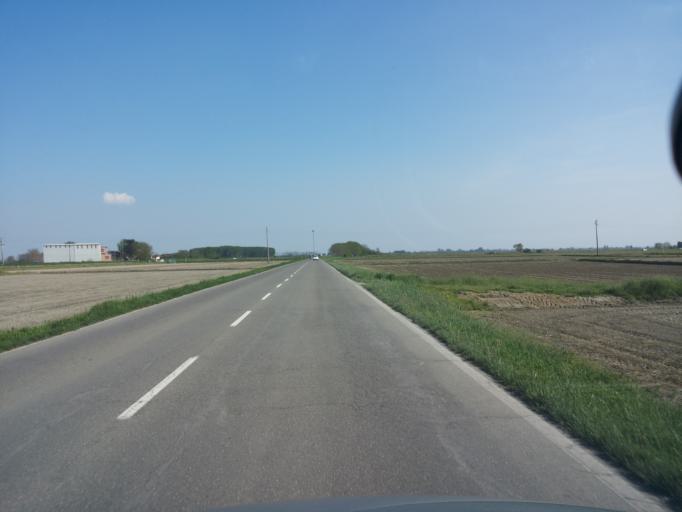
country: IT
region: Lombardy
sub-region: Provincia di Pavia
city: Cozzo
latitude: 45.1894
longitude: 8.5995
